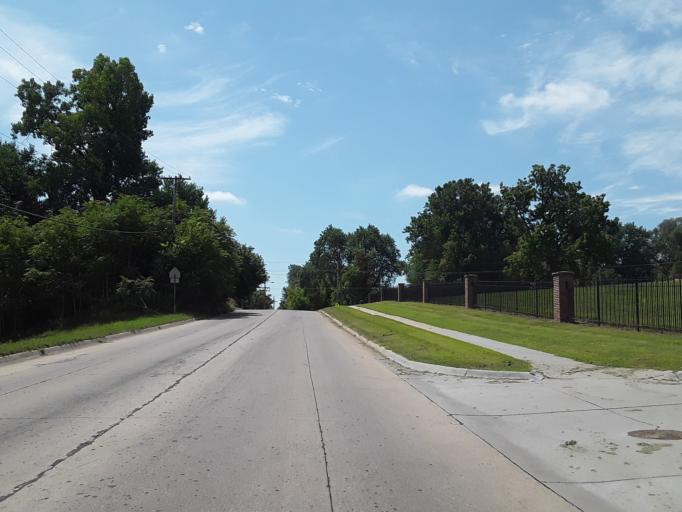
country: US
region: Nebraska
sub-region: Sarpy County
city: Bellevue
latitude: 41.1496
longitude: -95.8906
